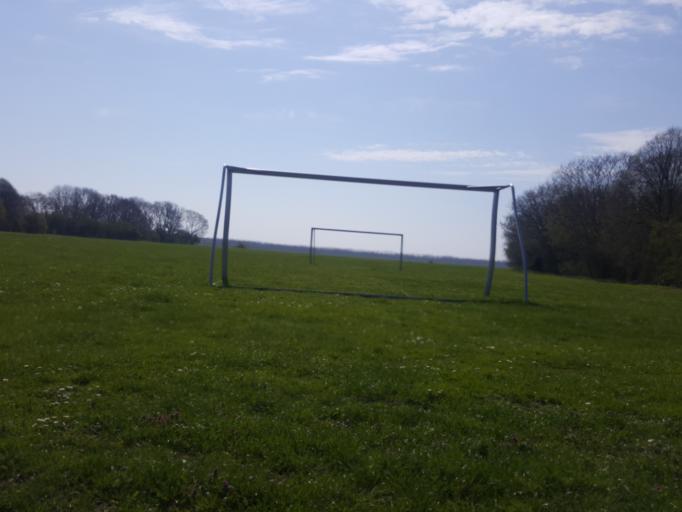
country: DK
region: Capital Region
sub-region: Frederiksberg Kommune
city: Frederiksberg
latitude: 55.6399
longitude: 12.5229
